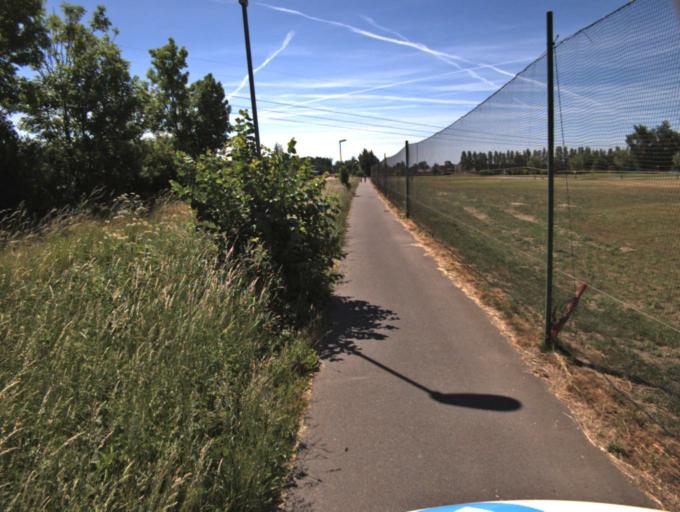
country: SE
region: Skane
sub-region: Kristianstads Kommun
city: Kristianstad
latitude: 56.0651
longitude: 14.0883
